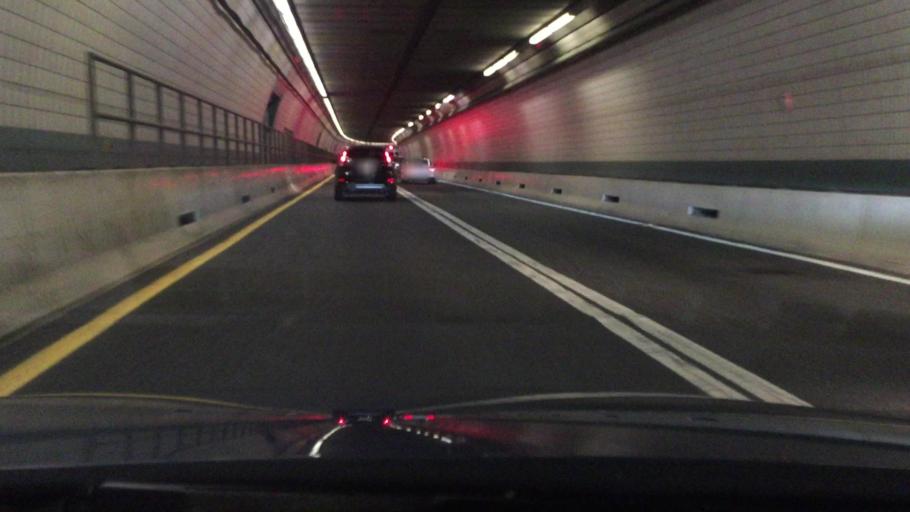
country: US
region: Massachusetts
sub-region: Suffolk County
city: Boston
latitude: 42.3545
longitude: -71.0353
